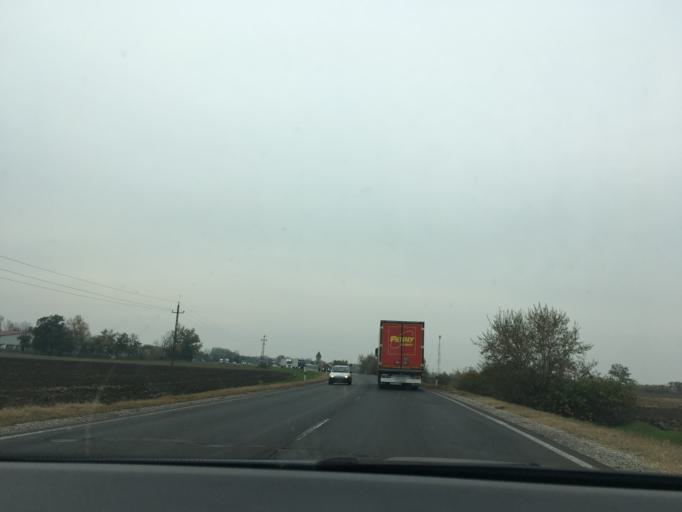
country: HU
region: Jasz-Nagykun-Szolnok
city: Fegyvernek
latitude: 47.2422
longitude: 20.5472
